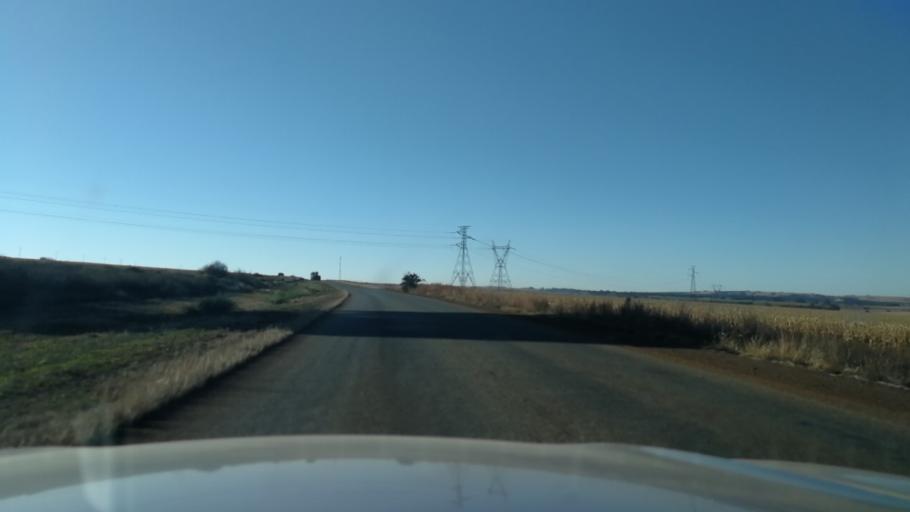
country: ZA
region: North-West
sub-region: Bojanala Platinum District Municipality
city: Rustenburg
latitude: -25.9959
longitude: 27.2970
